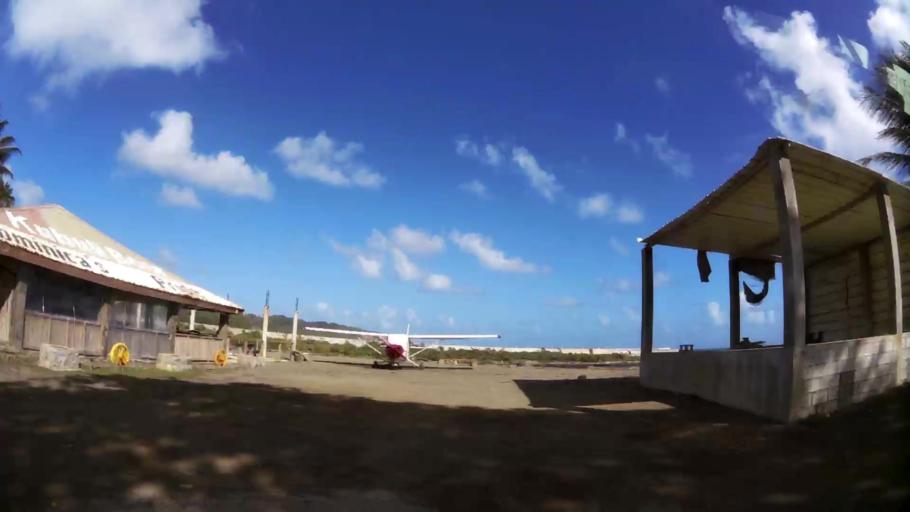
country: DM
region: Saint Andrew
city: Marigot
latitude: 15.5476
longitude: -61.2925
